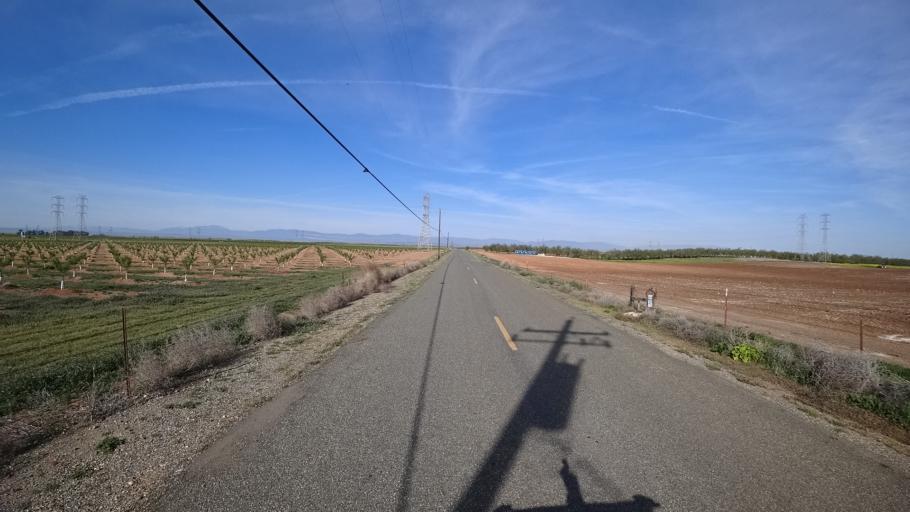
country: US
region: California
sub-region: Glenn County
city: Orland
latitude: 39.6684
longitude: -122.2624
